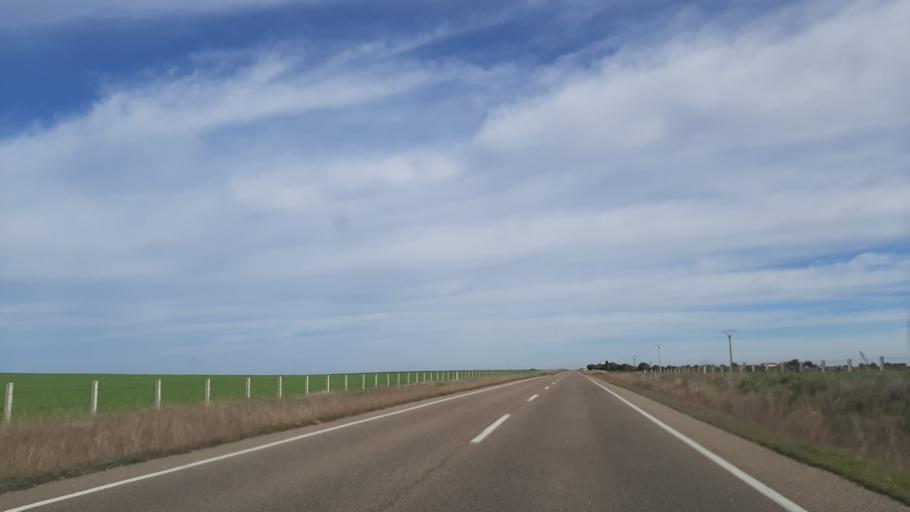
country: ES
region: Castille and Leon
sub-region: Provincia de Salamanca
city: Ledesma
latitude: 41.0904
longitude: -5.9765
